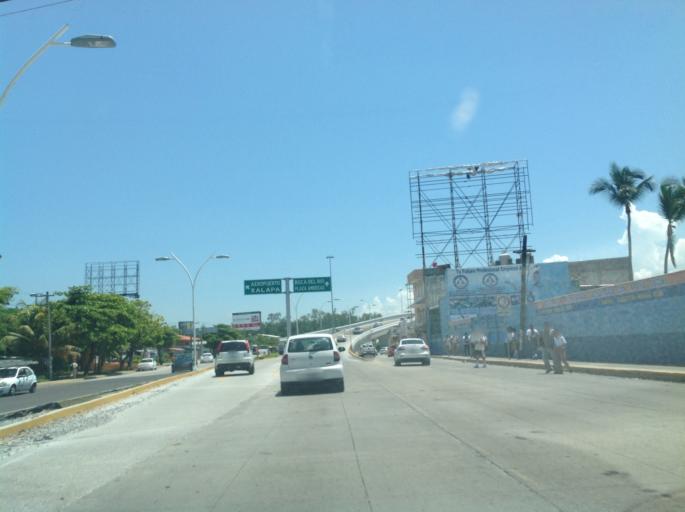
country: MX
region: Veracruz
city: Veracruz
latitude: 19.1496
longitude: -96.1295
